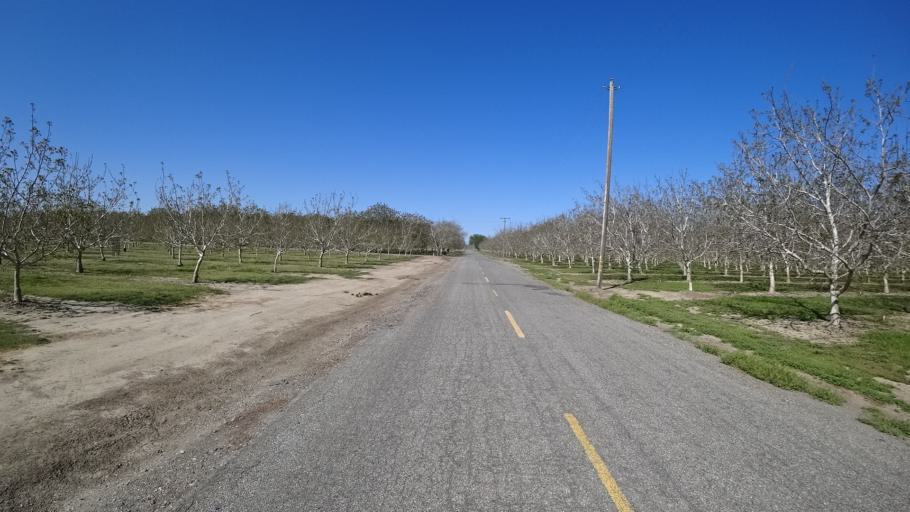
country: US
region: California
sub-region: Glenn County
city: Hamilton City
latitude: 39.7216
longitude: -122.0143
